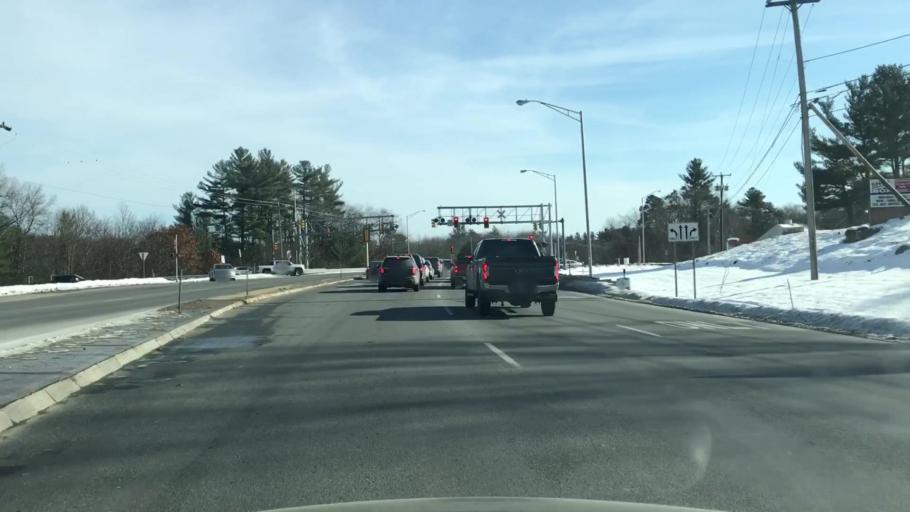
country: US
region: New Hampshire
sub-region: Hillsborough County
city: Milford
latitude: 42.8227
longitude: -71.6073
